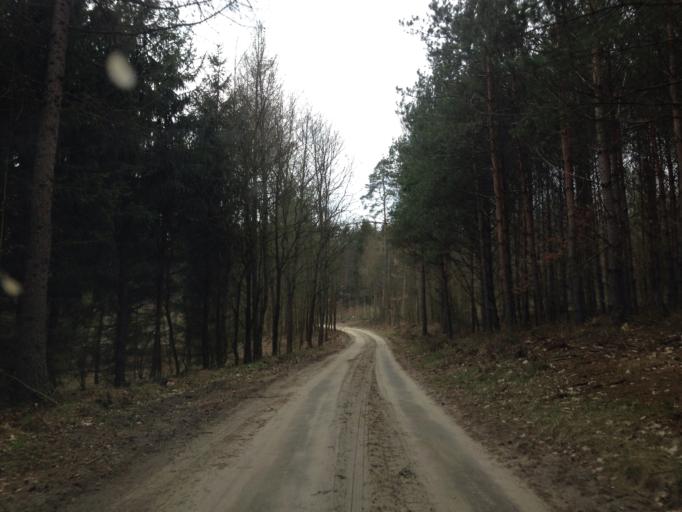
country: PL
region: Warmian-Masurian Voivodeship
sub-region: Powiat dzialdowski
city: Lidzbark
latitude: 53.2178
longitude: 19.7396
